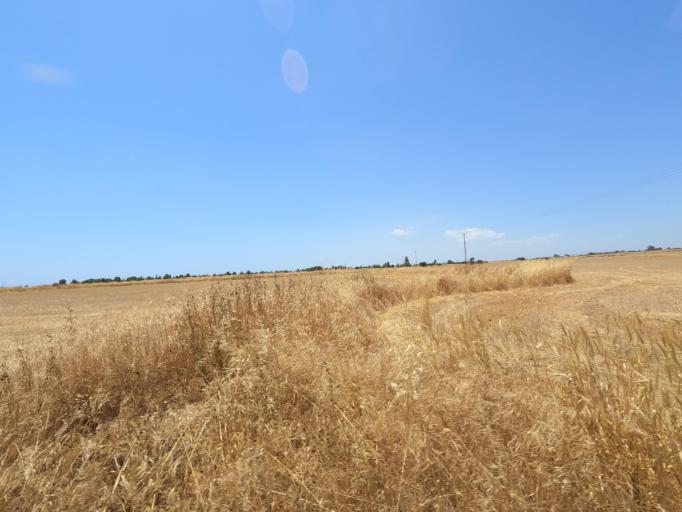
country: CY
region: Larnaka
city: Pergamos
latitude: 35.0213
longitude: 33.7164
